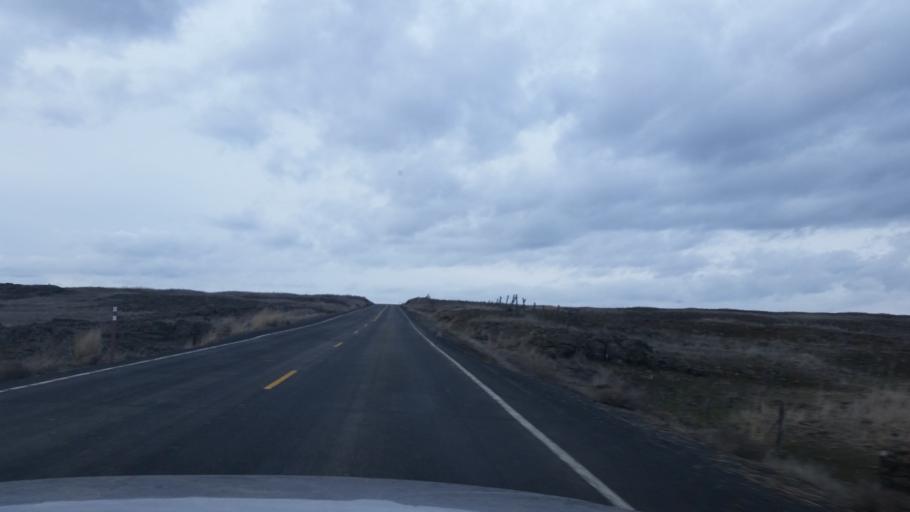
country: US
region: Washington
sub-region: Spokane County
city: Medical Lake
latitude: 47.2187
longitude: -117.8996
